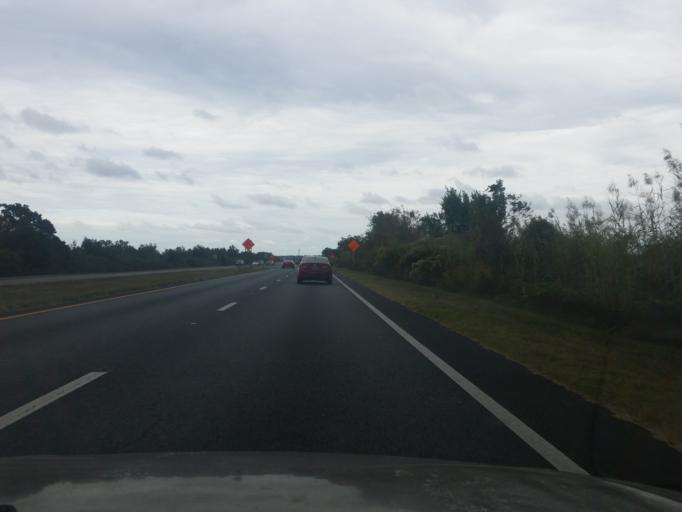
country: US
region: Florida
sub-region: Santa Rosa County
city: Pace
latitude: 30.5624
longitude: -87.1890
